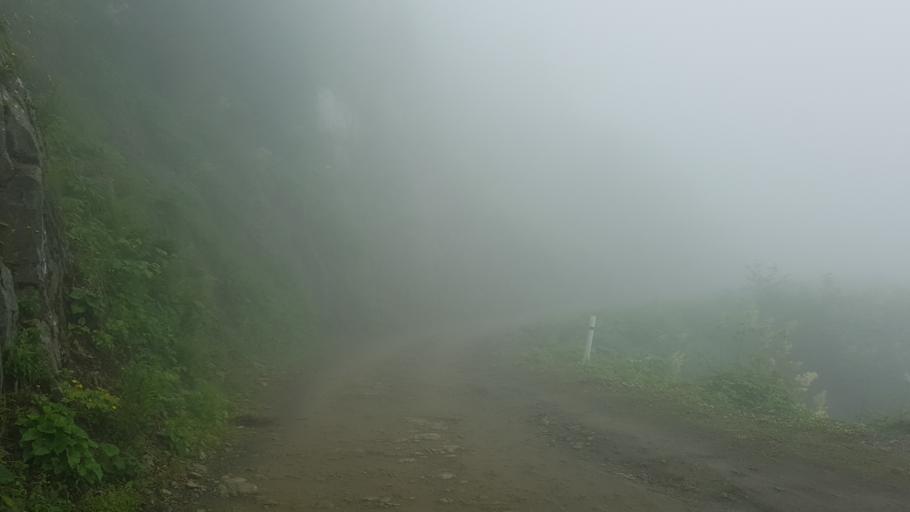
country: GE
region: Guria
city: Ozurgeti
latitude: 41.8331
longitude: 42.1522
